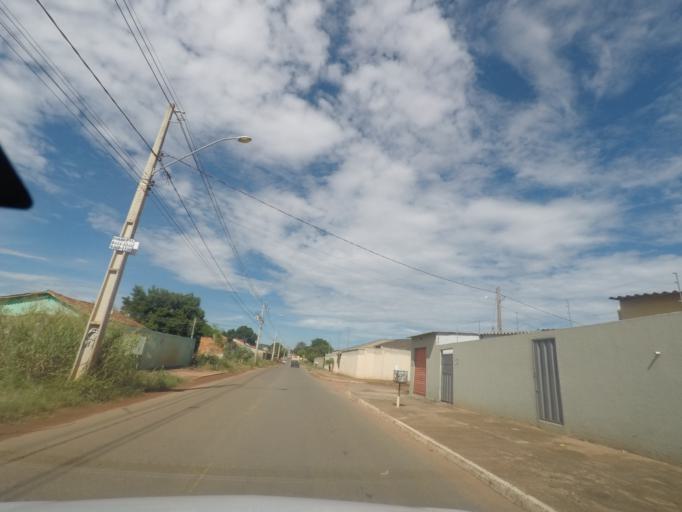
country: BR
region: Goias
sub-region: Aparecida De Goiania
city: Aparecida de Goiania
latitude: -16.8114
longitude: -49.2817
